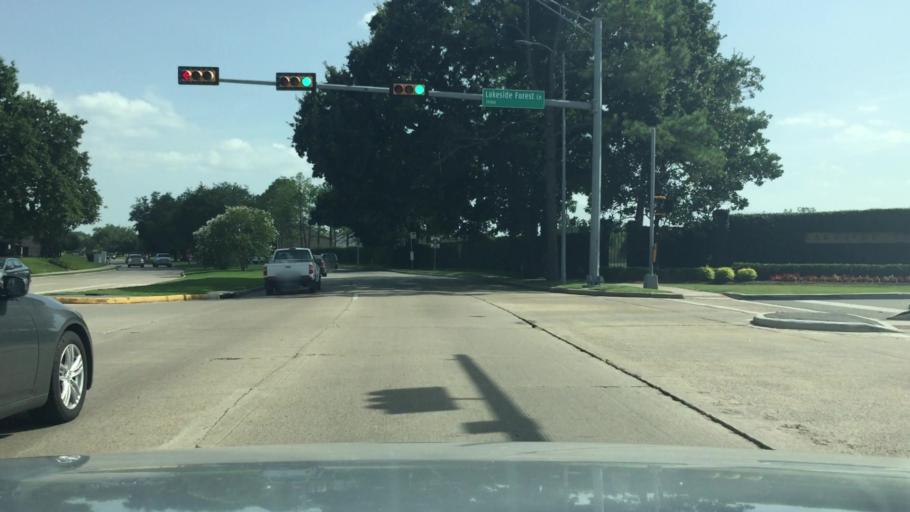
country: US
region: Texas
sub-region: Harris County
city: Bunker Hill Village
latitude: 29.7616
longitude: -95.5762
